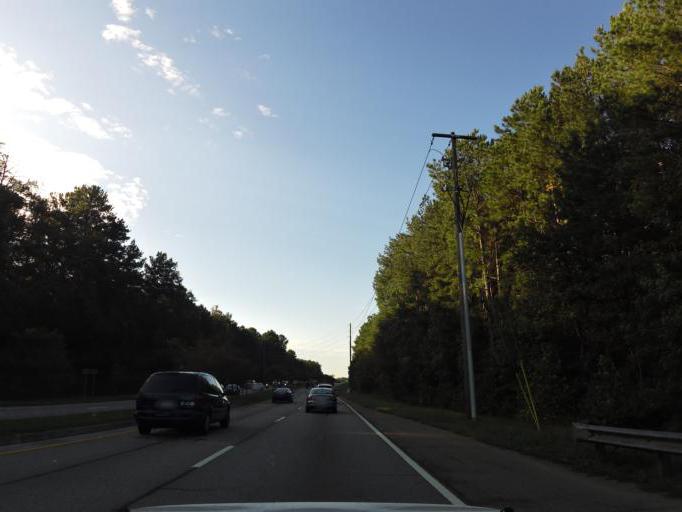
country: US
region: Georgia
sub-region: Cobb County
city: Powder Springs
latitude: 33.9113
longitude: -84.6275
